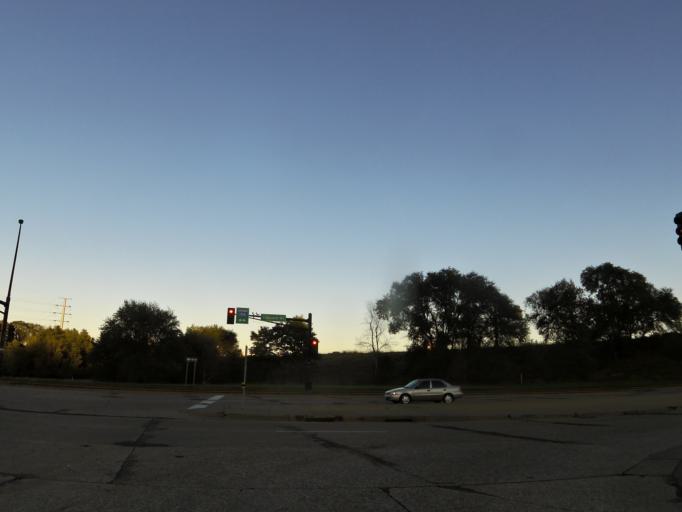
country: US
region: Minnesota
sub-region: Dakota County
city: South Saint Paul
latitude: 44.8770
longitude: -93.0314
